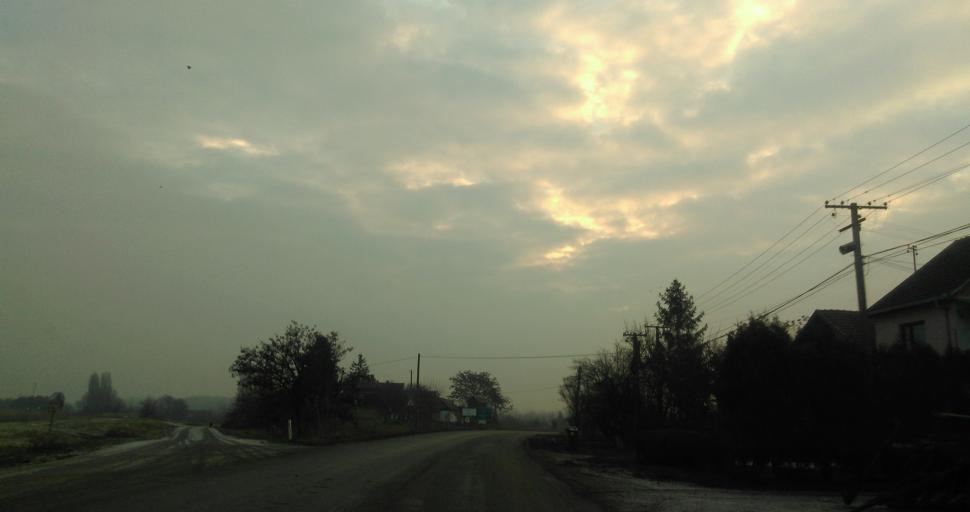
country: RS
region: Autonomna Pokrajina Vojvodina
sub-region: Juznobacki Okrug
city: Becej
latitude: 45.5997
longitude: 20.0442
